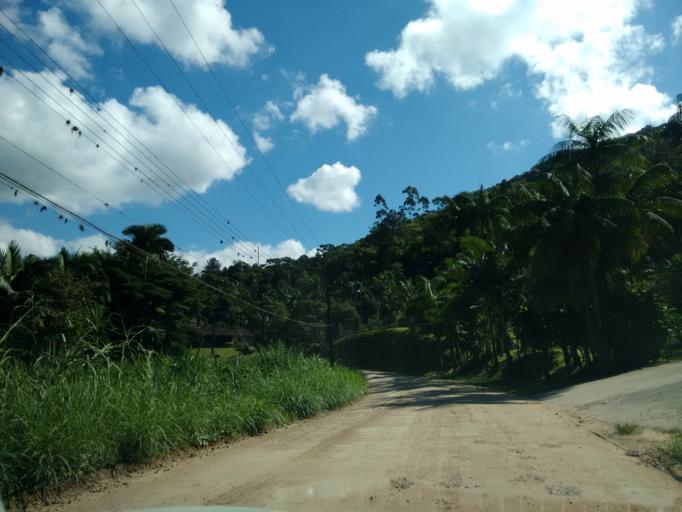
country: BR
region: Santa Catarina
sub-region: Pomerode
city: Pomerode
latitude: -26.8210
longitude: -49.1766
